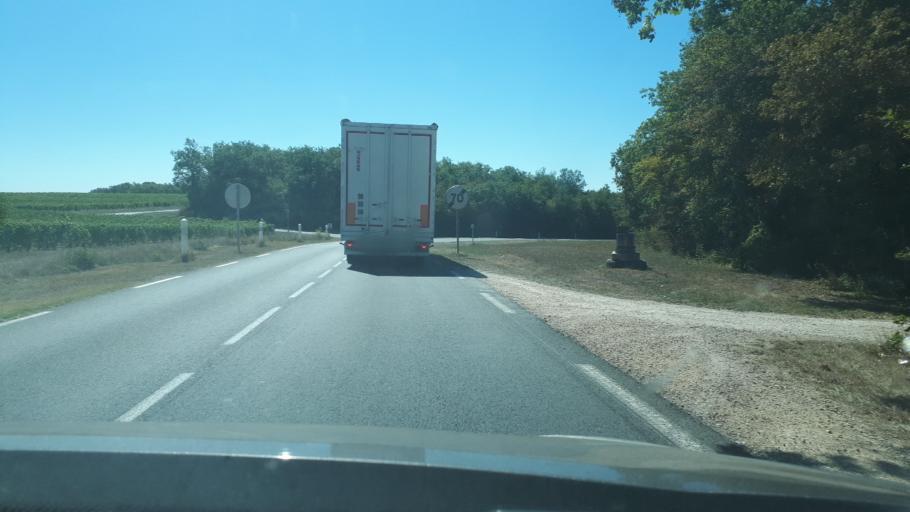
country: FR
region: Centre
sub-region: Departement du Cher
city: Sancerre
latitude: 47.3126
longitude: 2.8100
